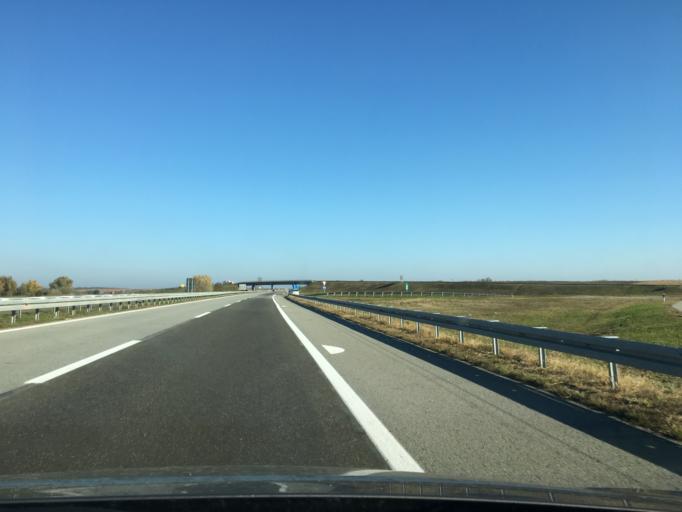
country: RS
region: Autonomna Pokrajina Vojvodina
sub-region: Severnobacki Okrug
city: Mali Igos
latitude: 45.6395
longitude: 19.7122
